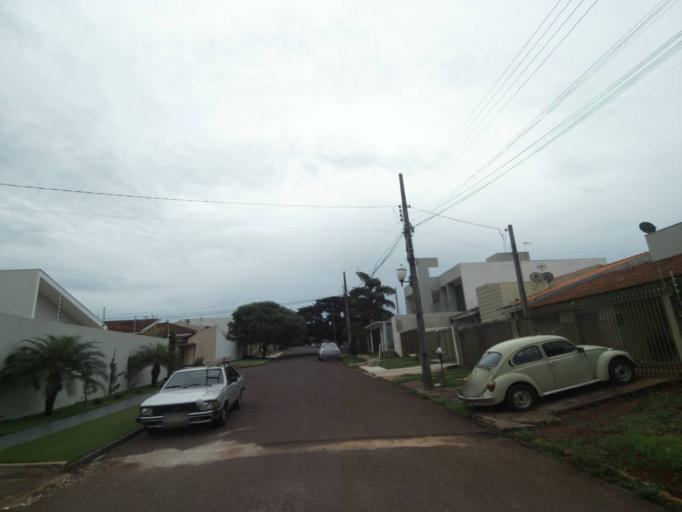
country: BR
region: Parana
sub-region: Campo Mourao
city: Campo Mourao
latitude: -24.0302
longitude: -52.3580
